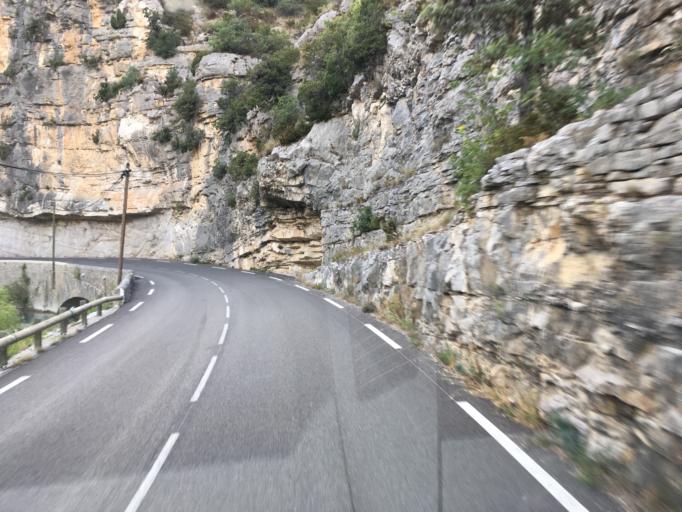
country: FR
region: Rhone-Alpes
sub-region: Departement de la Drome
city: Buis-les-Baronnies
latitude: 44.4332
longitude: 5.2833
